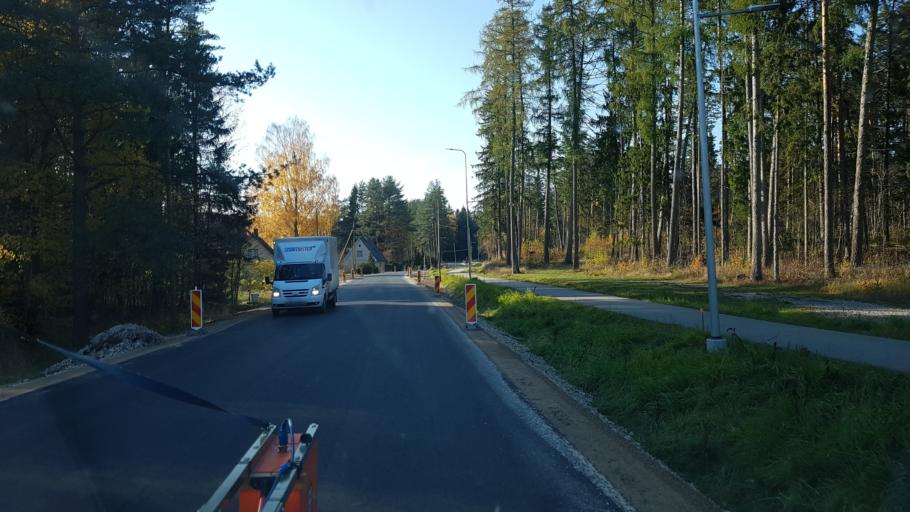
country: EE
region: Vorumaa
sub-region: Antsla vald
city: Vana-Antsla
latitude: 57.8309
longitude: 26.5191
